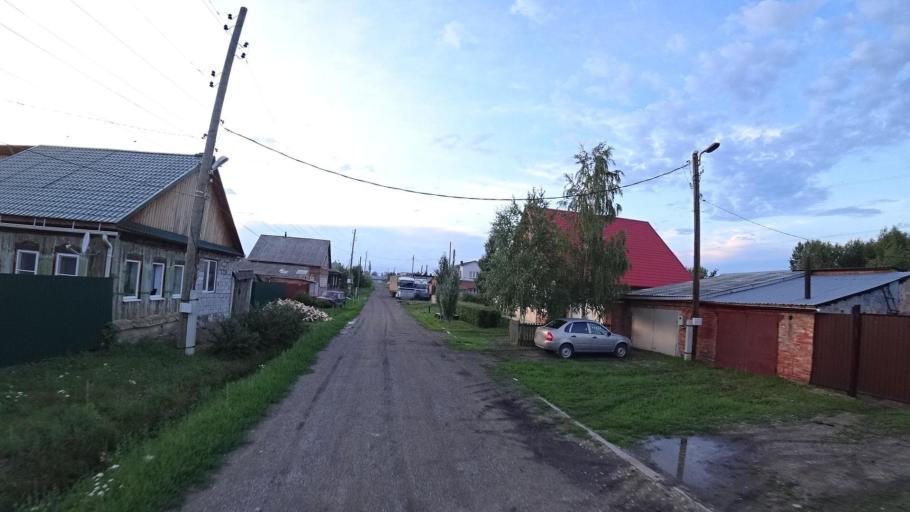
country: RU
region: Sverdlovsk
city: Kamyshlov
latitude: 56.8603
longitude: 62.7134
